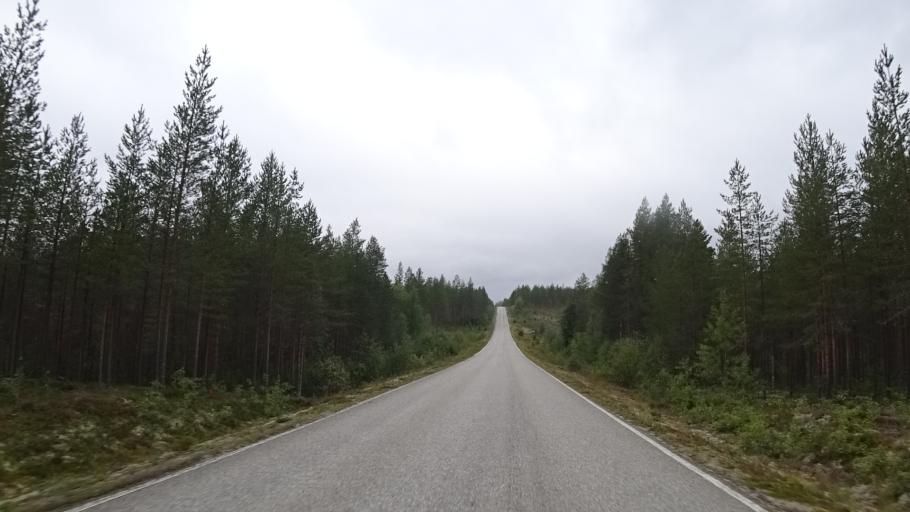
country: FI
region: North Karelia
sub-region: Pielisen Karjala
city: Lieksa
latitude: 63.3813
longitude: 30.3208
